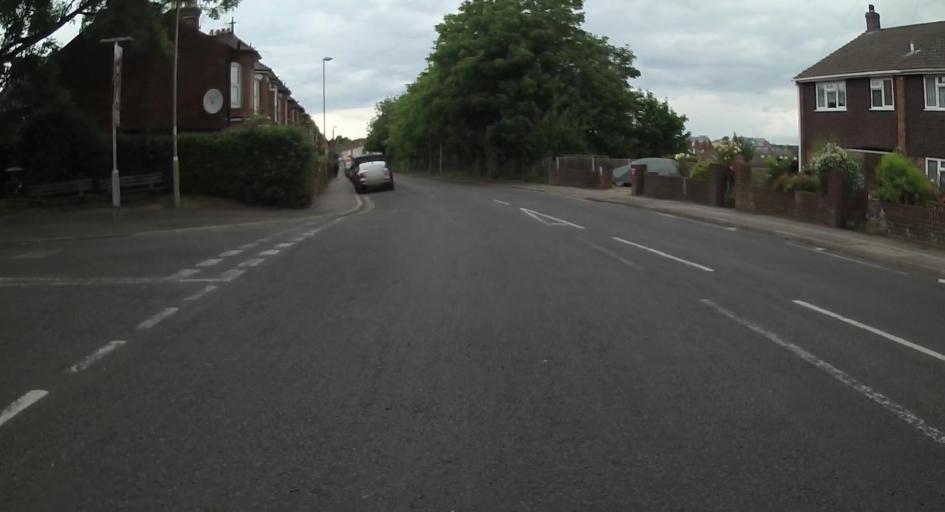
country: GB
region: England
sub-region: Hampshire
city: Aldershot
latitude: 51.2437
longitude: -0.7651
